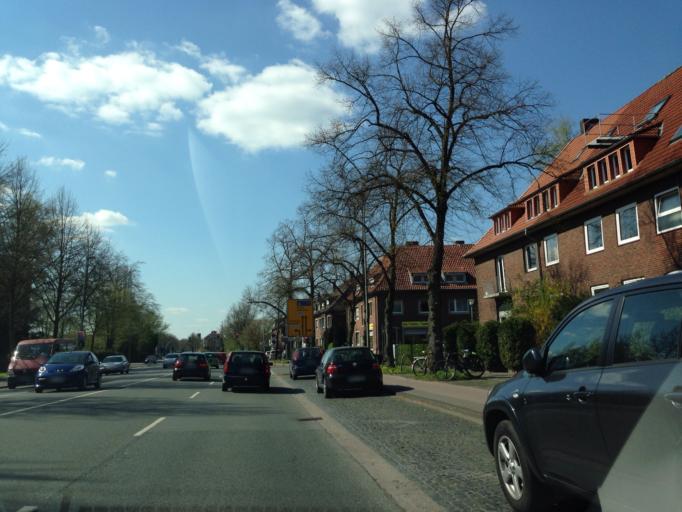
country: DE
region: North Rhine-Westphalia
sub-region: Regierungsbezirk Munster
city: Muenster
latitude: 51.9719
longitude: 7.6389
